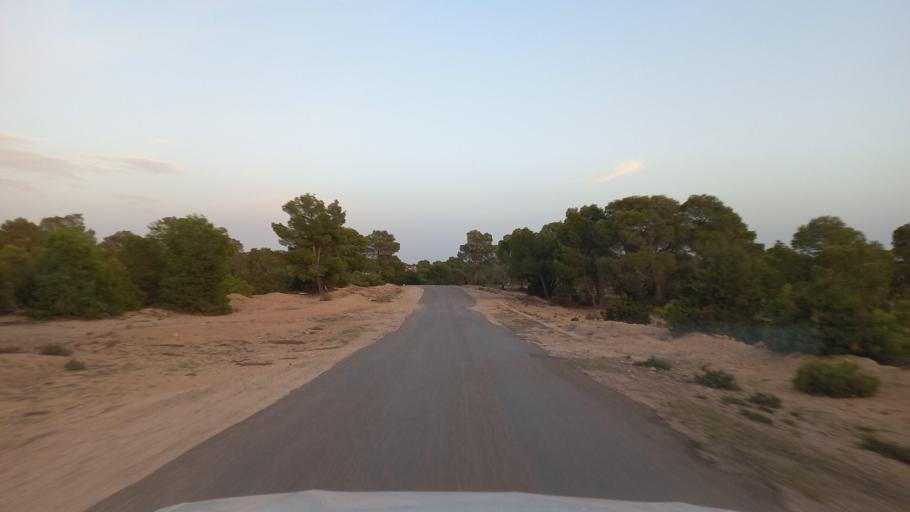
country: TN
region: Al Qasrayn
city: Sbiba
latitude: 35.4095
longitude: 8.9479
